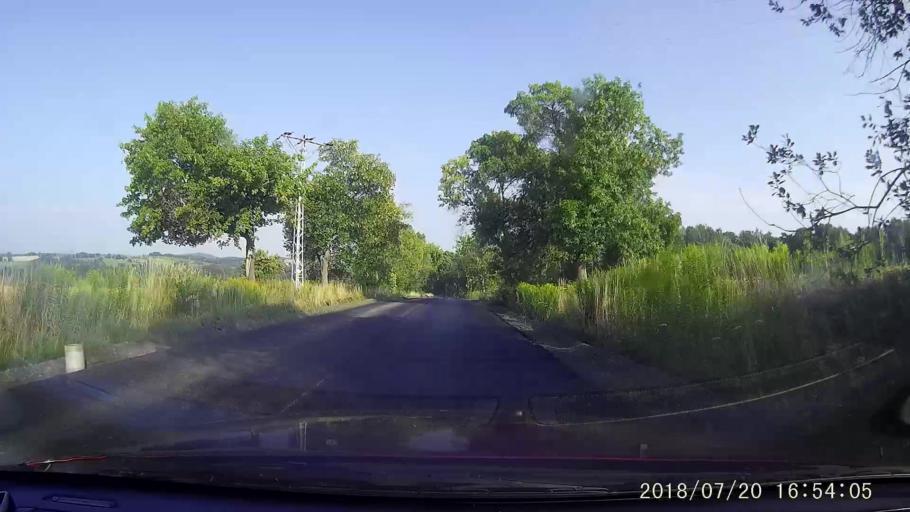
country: PL
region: Lower Silesian Voivodeship
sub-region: Powiat lubanski
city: Lesna
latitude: 51.0338
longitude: 15.2474
